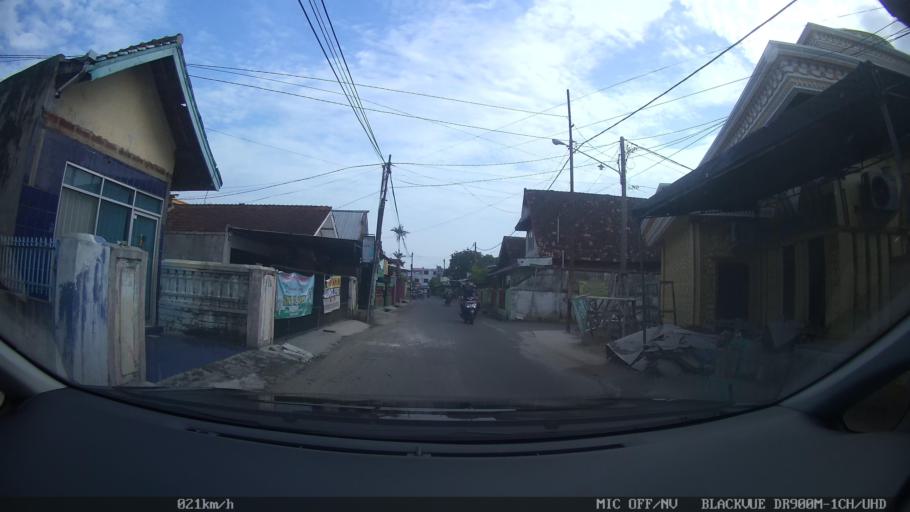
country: ID
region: Lampung
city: Bandarlampung
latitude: -5.4111
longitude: 105.2657
